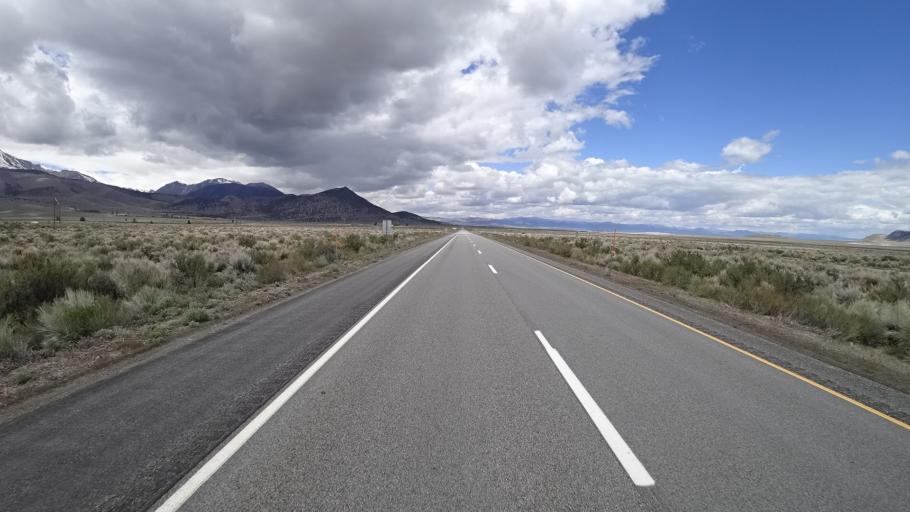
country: US
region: California
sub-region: Mono County
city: Mammoth Lakes
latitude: 37.8800
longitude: -119.0900
